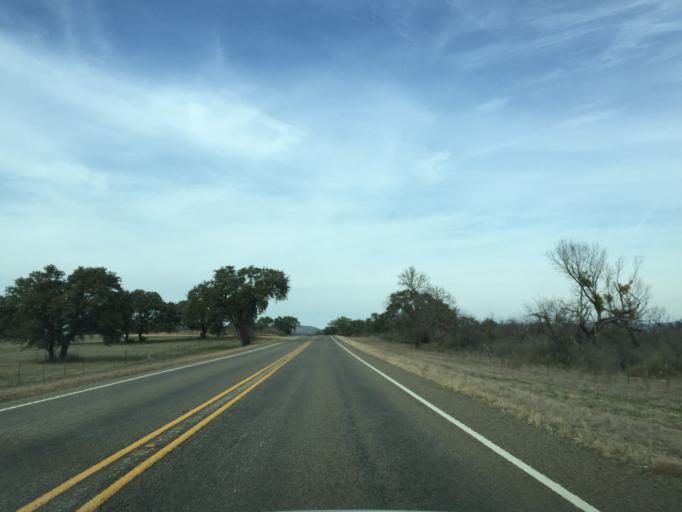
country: US
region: Texas
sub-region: Llano County
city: Llano
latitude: 30.5169
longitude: -98.7073
